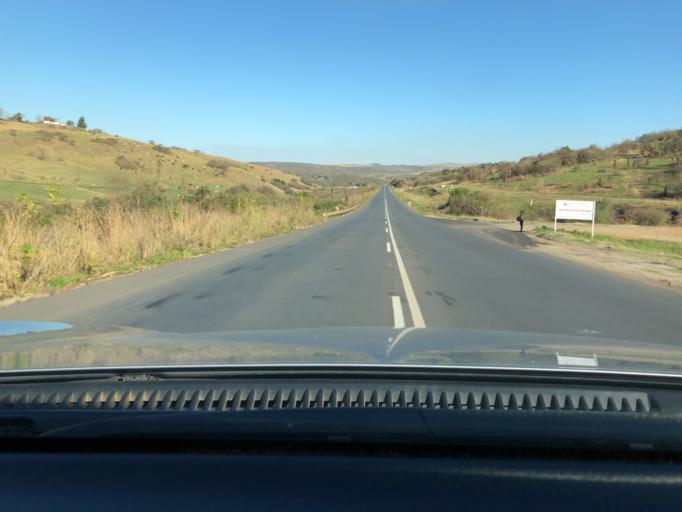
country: ZA
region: KwaZulu-Natal
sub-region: uMgungundlovu District Municipality
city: Camperdown
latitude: -29.7879
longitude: 30.5093
